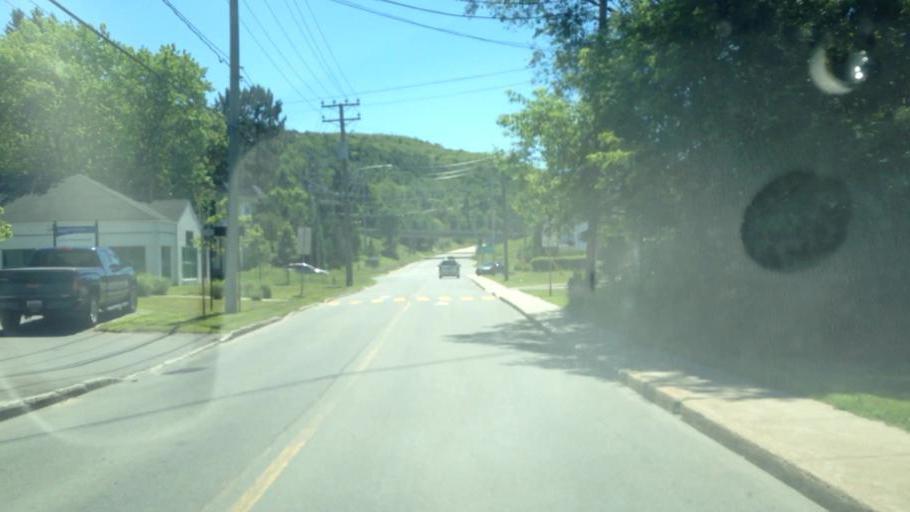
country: CA
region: Quebec
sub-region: Laurentides
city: Mont-Tremblant
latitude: 46.1158
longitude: -74.5959
